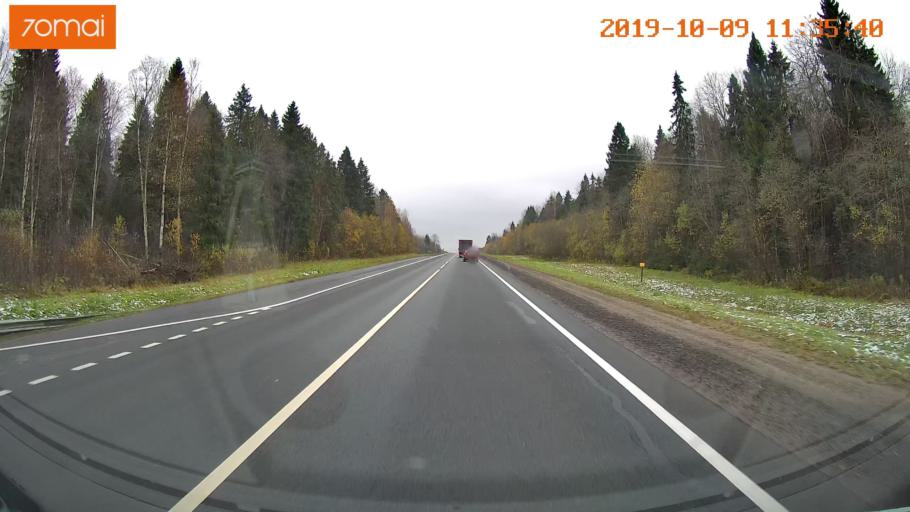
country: RU
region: Vologda
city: Gryazovets
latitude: 59.0004
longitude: 40.1285
